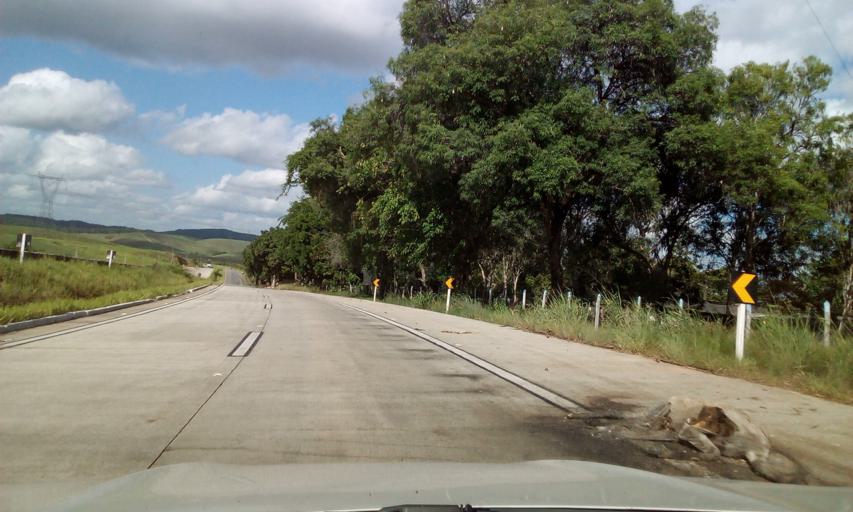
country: BR
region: Alagoas
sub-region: Novo Lino
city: Novo Lino
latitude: -8.9346
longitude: -35.6434
